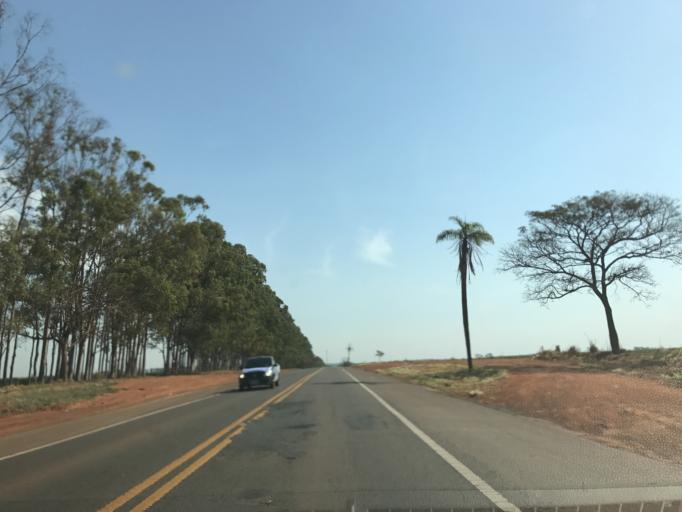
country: BR
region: Sao Paulo
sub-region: Jose Bonifacio
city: Jose Bonifacio
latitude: -21.1360
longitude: -49.8671
